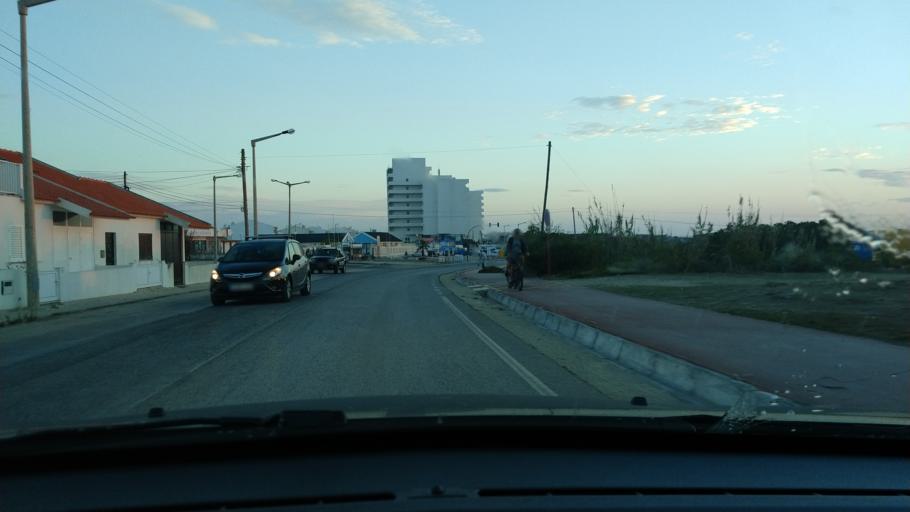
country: PT
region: Leiria
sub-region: Peniche
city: Atouguia da Baleia
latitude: 39.3672
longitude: -9.3367
